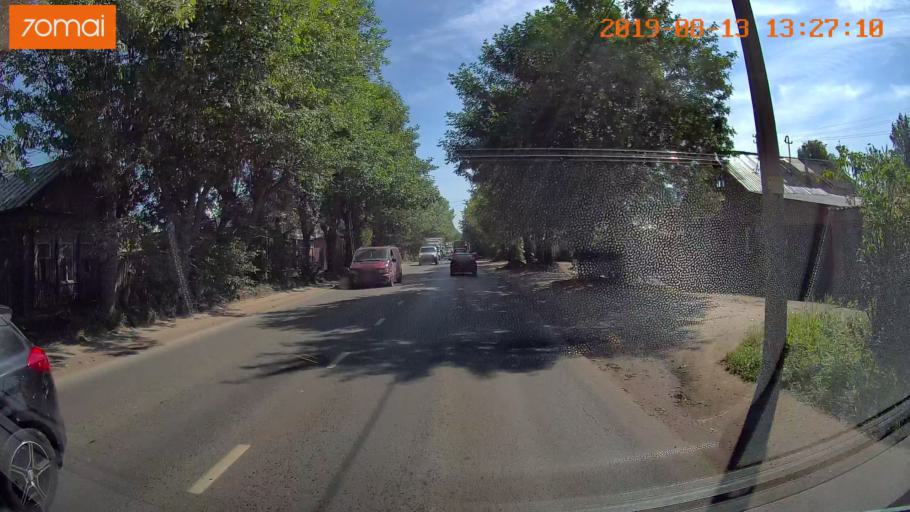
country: RU
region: Ivanovo
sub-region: Gorod Ivanovo
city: Ivanovo
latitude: 56.9963
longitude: 40.9510
